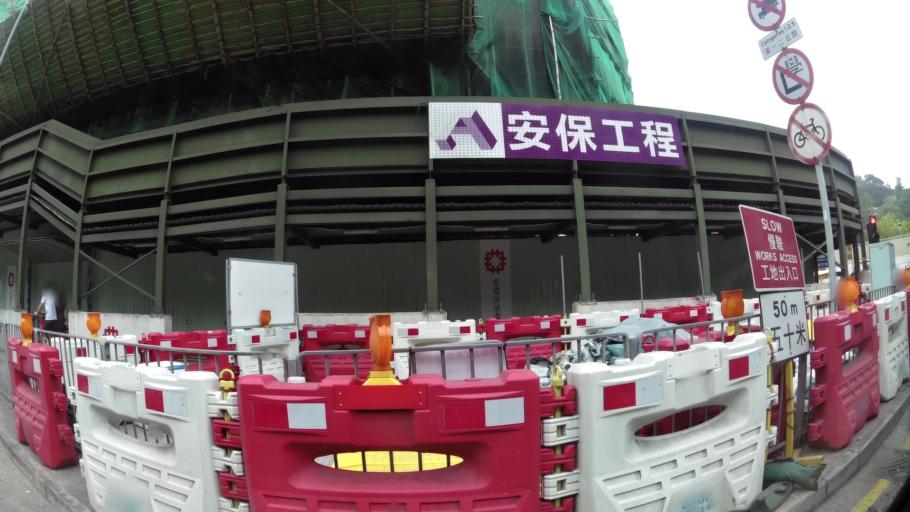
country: HK
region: Kowloon City
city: Kowloon
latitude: 22.3031
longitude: 114.2365
